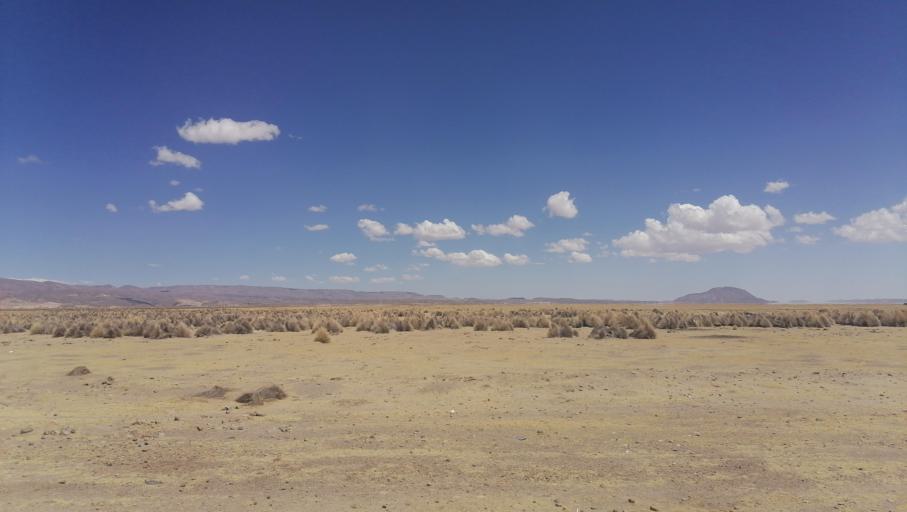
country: BO
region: Oruro
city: Challapata
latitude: -19.1719
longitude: -66.7987
